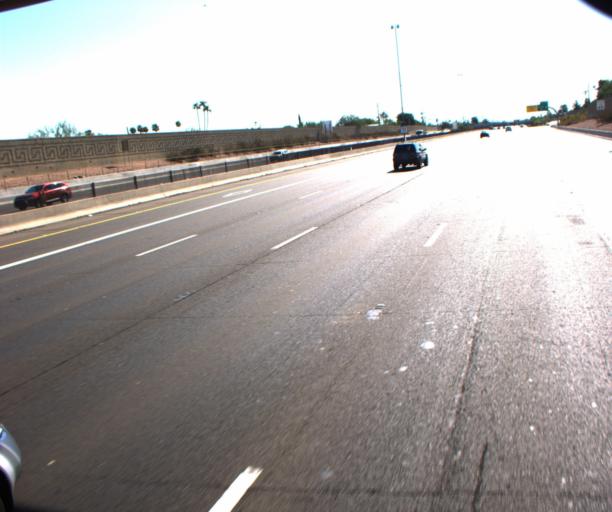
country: US
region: Arizona
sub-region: Maricopa County
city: Tempe Junction
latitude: 33.3854
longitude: -111.9342
